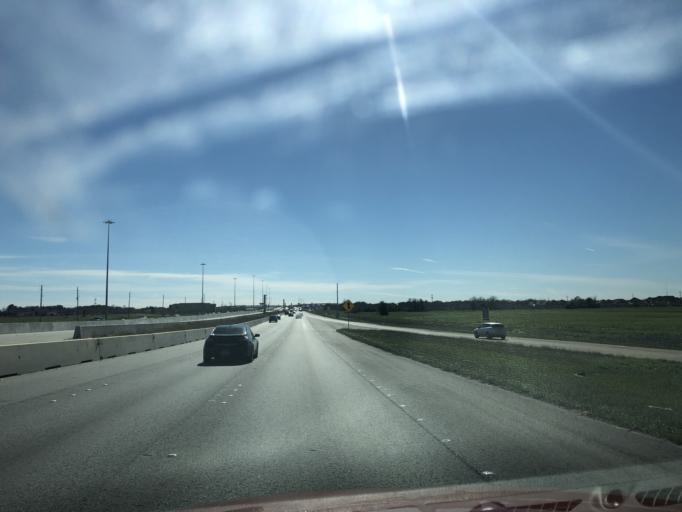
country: US
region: Texas
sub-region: Brazoria County
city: Brookside Village
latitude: 29.6253
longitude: -95.3873
